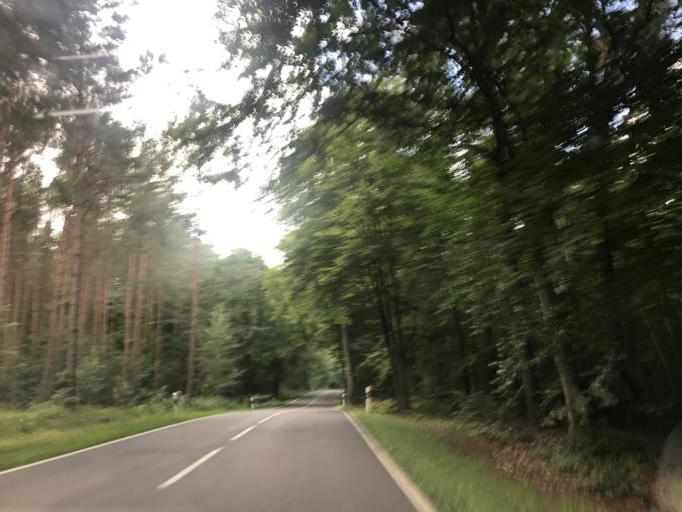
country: DE
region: Brandenburg
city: Rheinsberg
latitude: 53.1115
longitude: 12.9964
